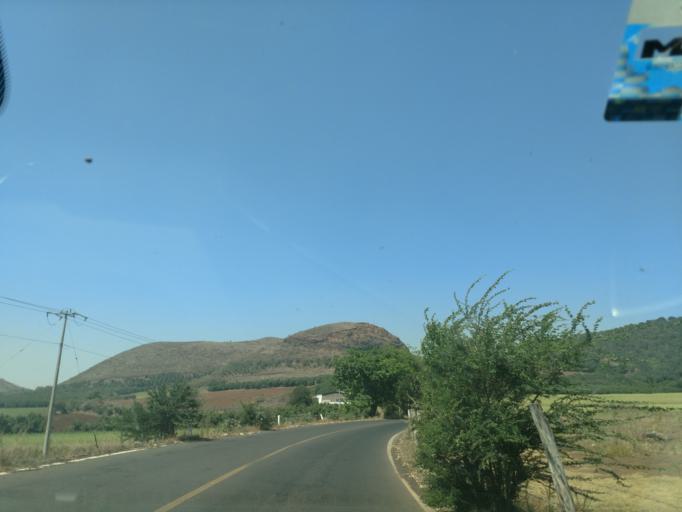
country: MX
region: Nayarit
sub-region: Tepic
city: La Corregidora
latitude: 21.4978
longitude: -104.7808
